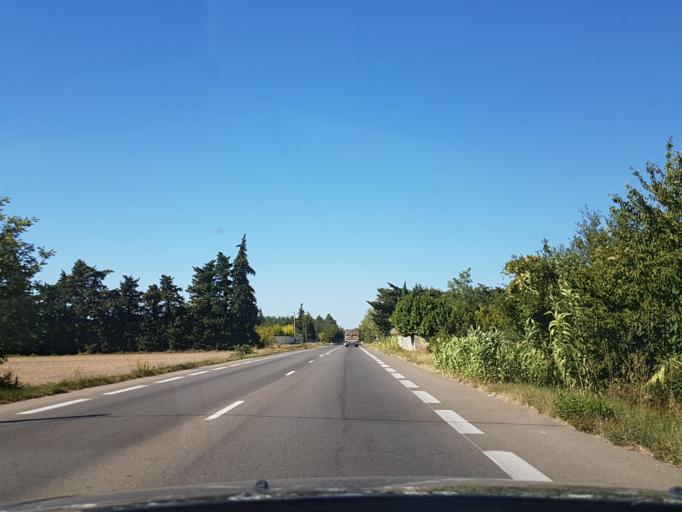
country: FR
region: Provence-Alpes-Cote d'Azur
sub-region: Departement du Vaucluse
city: L'Isle-sur-la-Sorgue
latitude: 43.9325
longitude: 5.0305
